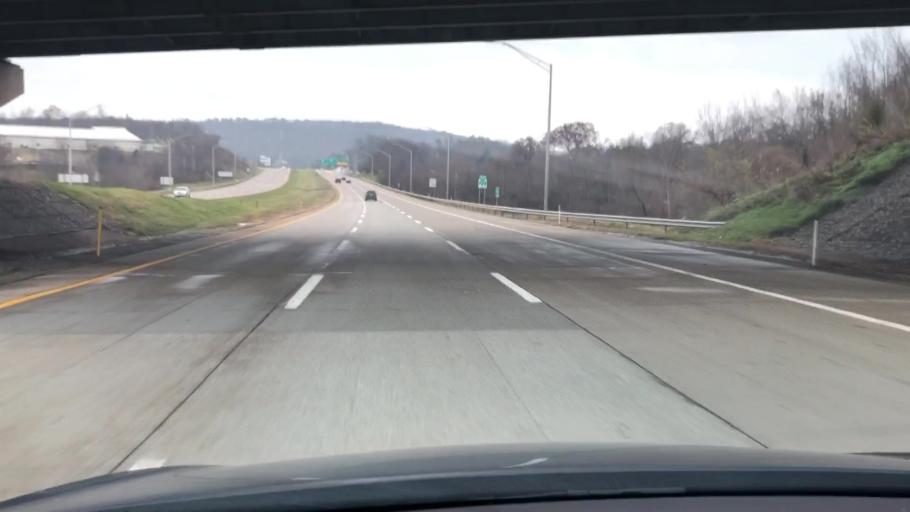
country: US
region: Pennsylvania
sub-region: Westmoreland County
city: New Stanton
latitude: 40.2328
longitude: -79.6013
